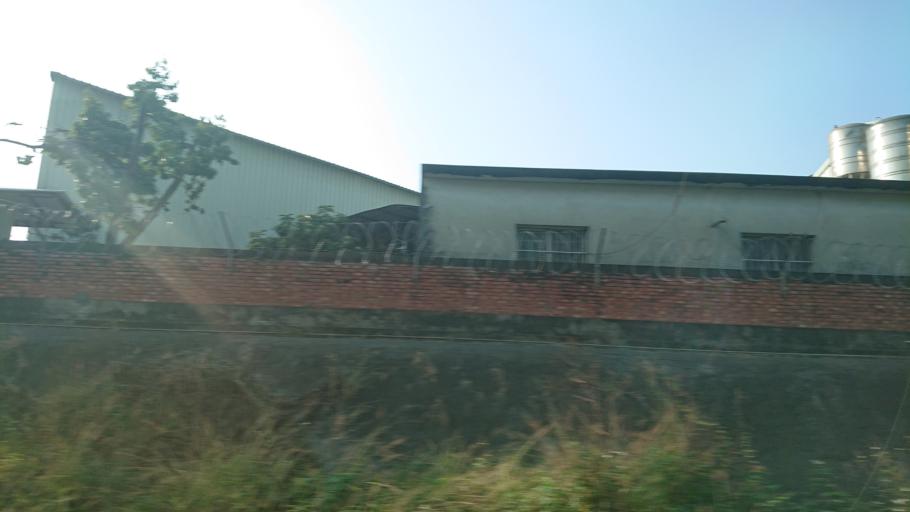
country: TW
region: Taiwan
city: Xinying
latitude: 23.1676
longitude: 120.2536
